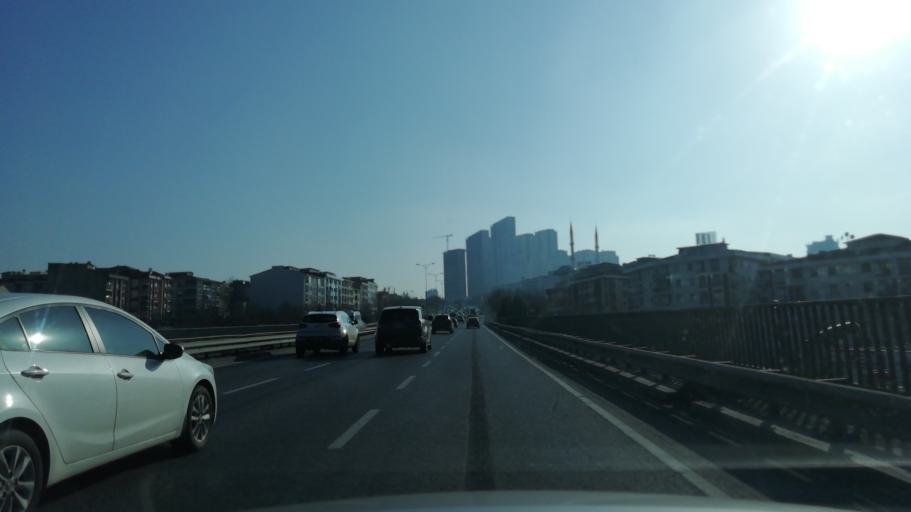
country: TR
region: Istanbul
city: Esenyurt
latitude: 41.0407
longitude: 28.6896
